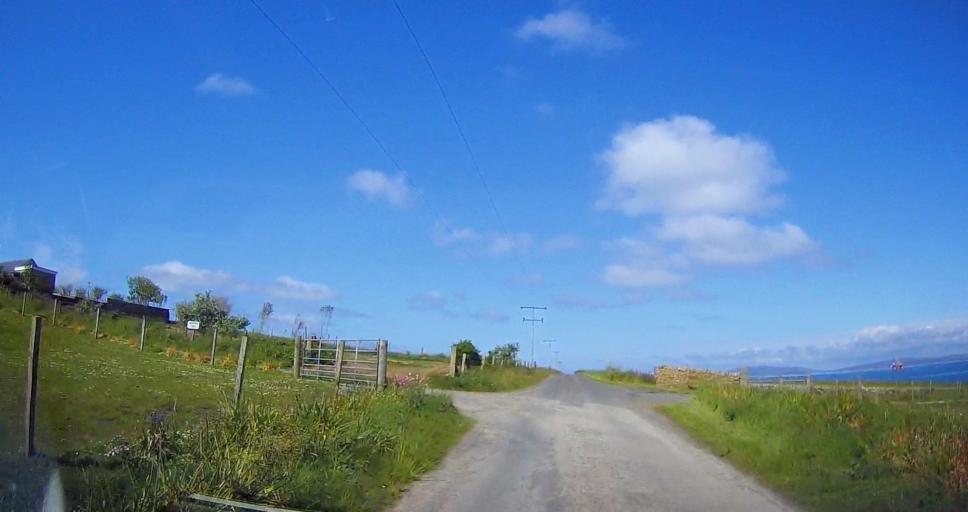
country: GB
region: Scotland
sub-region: Orkney Islands
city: Kirkwall
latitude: 58.8554
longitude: -2.9284
